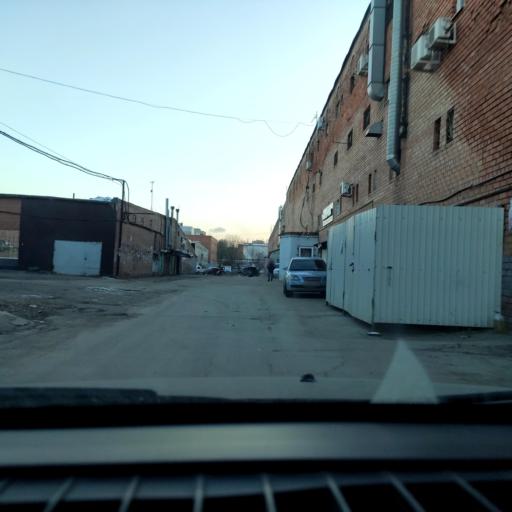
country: RU
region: Samara
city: Tol'yatti
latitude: 53.5401
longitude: 49.2902
